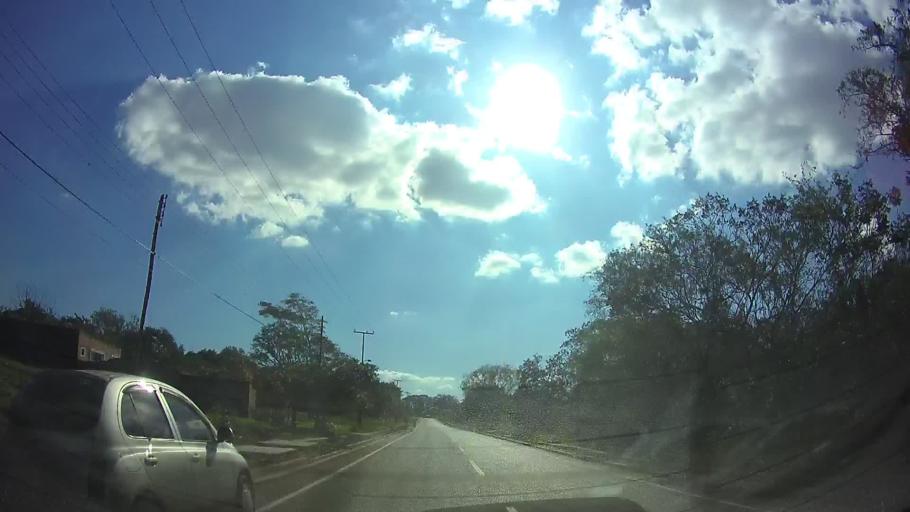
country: PY
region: Central
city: San Lorenzo
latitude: -25.2696
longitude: -57.4659
